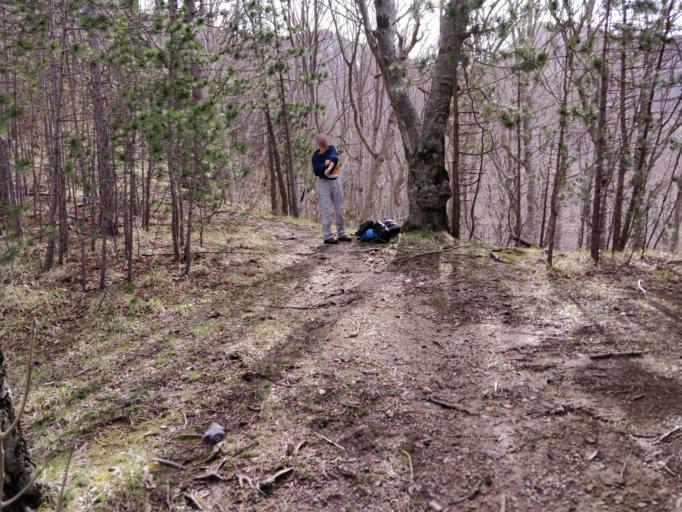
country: HR
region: Zadarska
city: Starigrad
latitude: 44.3309
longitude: 15.5290
